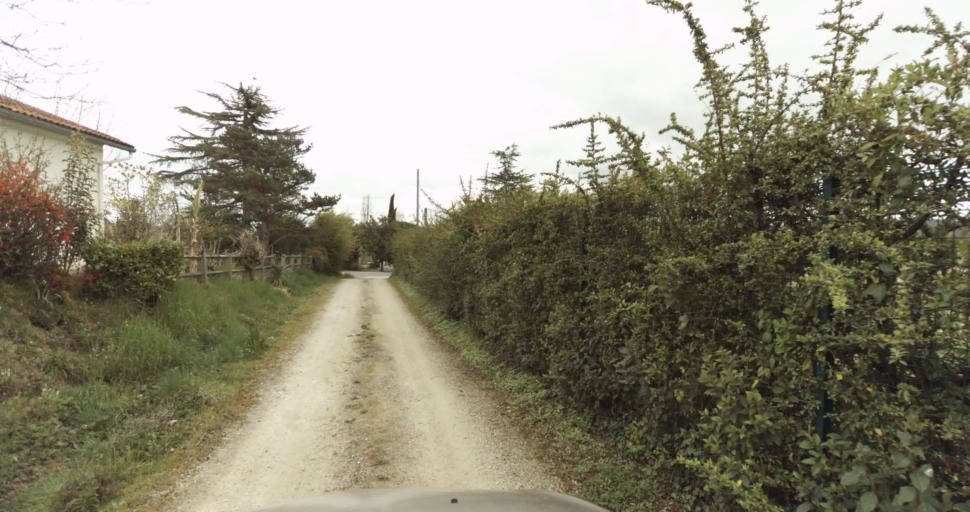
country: FR
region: Midi-Pyrenees
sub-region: Departement du Tarn
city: Puygouzon
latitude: 43.9092
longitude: 2.1677
